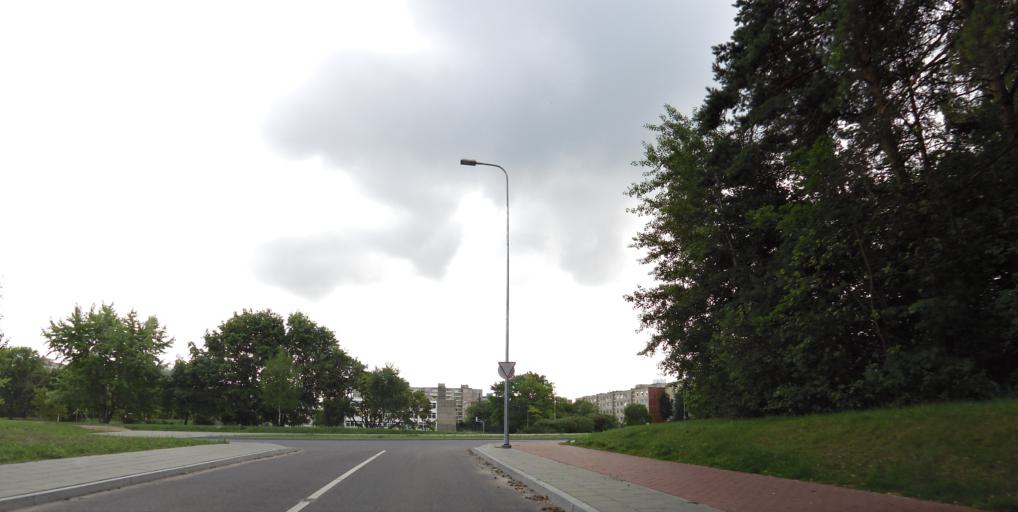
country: LT
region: Vilnius County
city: Pilaite
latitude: 54.6948
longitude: 25.2073
